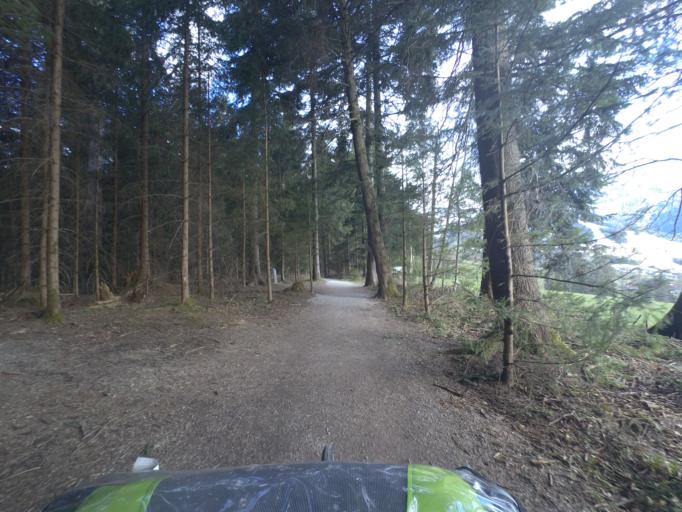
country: AT
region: Salzburg
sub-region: Politischer Bezirk Hallein
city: Abtenau
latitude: 47.5715
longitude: 13.3499
